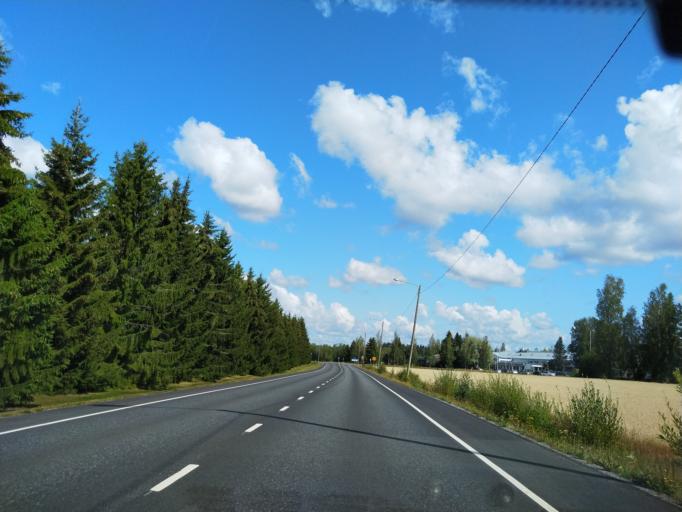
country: FI
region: Satakunta
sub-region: Pori
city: Huittinen
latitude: 61.1771
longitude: 22.7122
